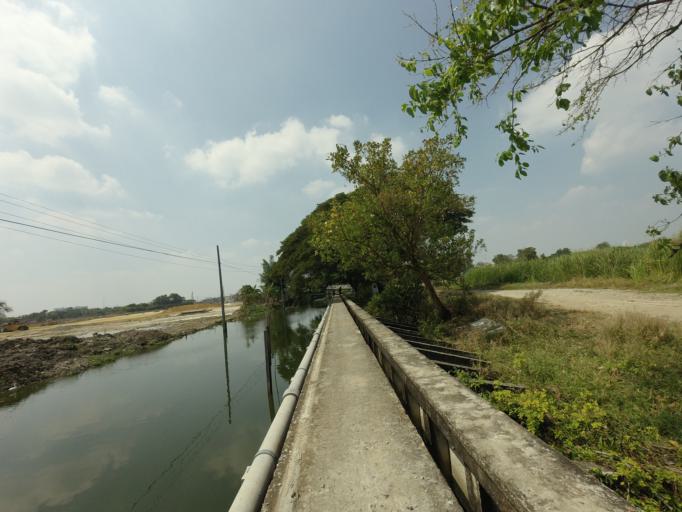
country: TH
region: Bangkok
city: Suan Luang
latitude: 13.7493
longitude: 100.6635
